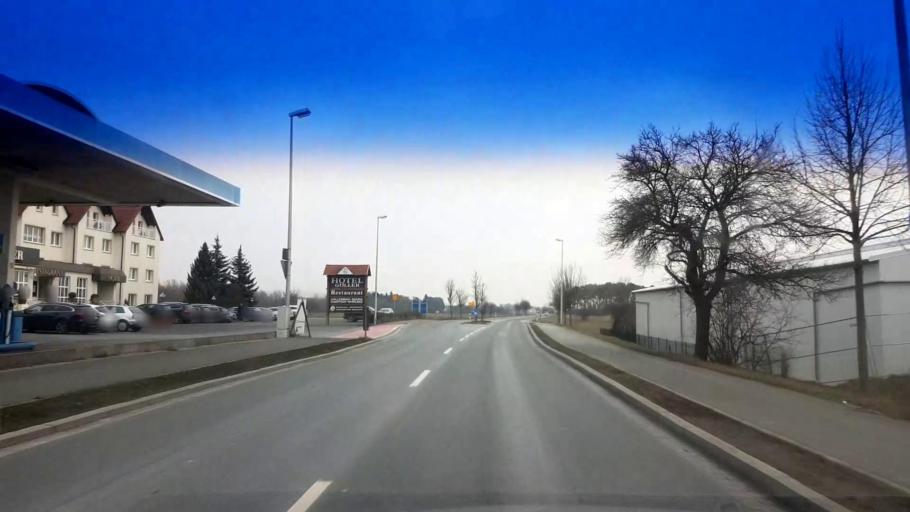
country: DE
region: Bavaria
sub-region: Upper Franconia
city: Hirschaid
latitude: 49.8113
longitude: 10.9976
